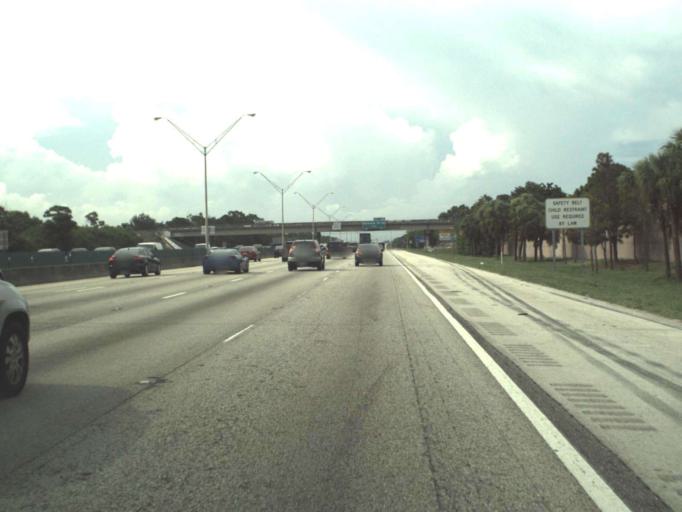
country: US
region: Florida
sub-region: Broward County
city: Deerfield Beach
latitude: 26.3295
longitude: -80.1168
